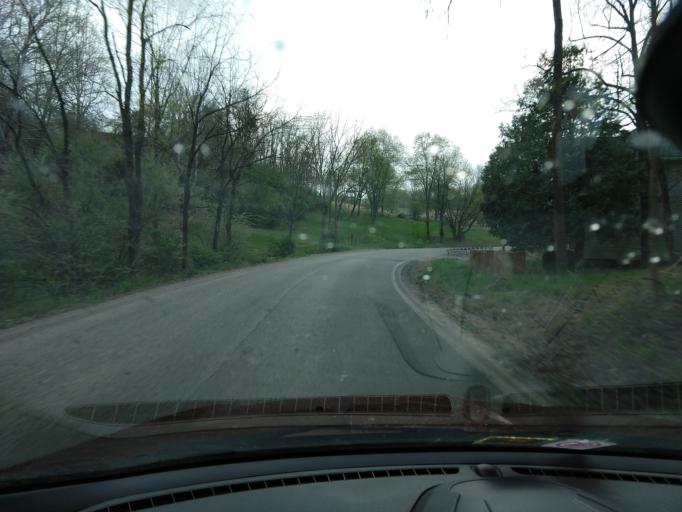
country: US
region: West Virginia
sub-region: Harrison County
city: Bridgeport
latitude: 39.3392
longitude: -80.2684
